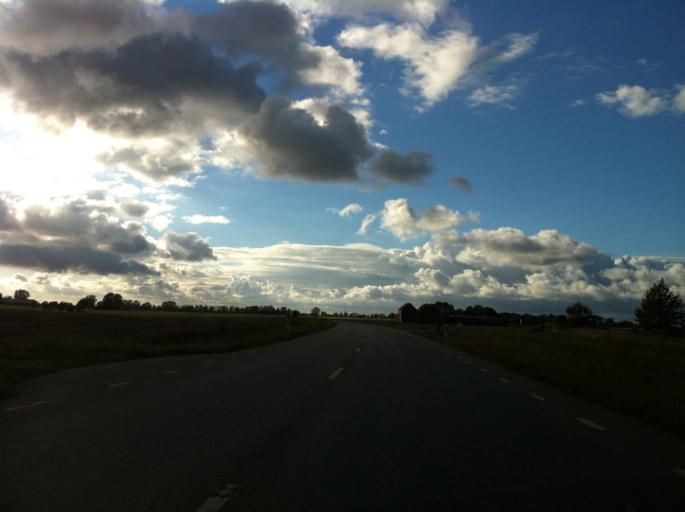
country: SE
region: Skane
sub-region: Svalovs Kommun
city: Teckomatorp
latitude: 55.8783
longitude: 13.0456
